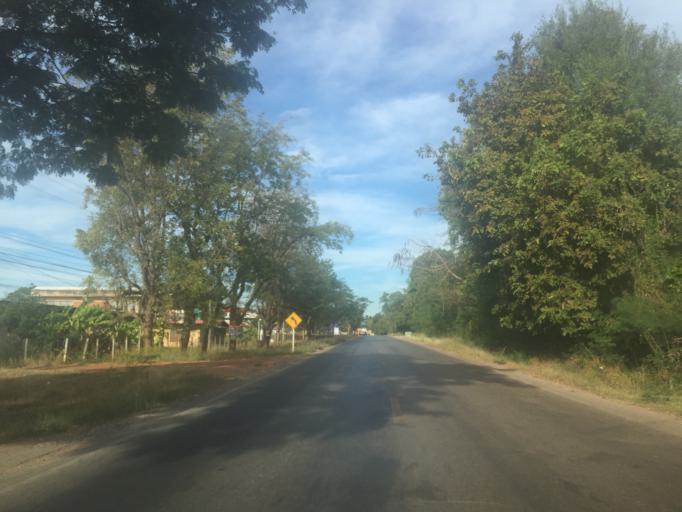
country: TH
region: Changwat Udon Thani
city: Si That
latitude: 16.9727
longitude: 103.2305
